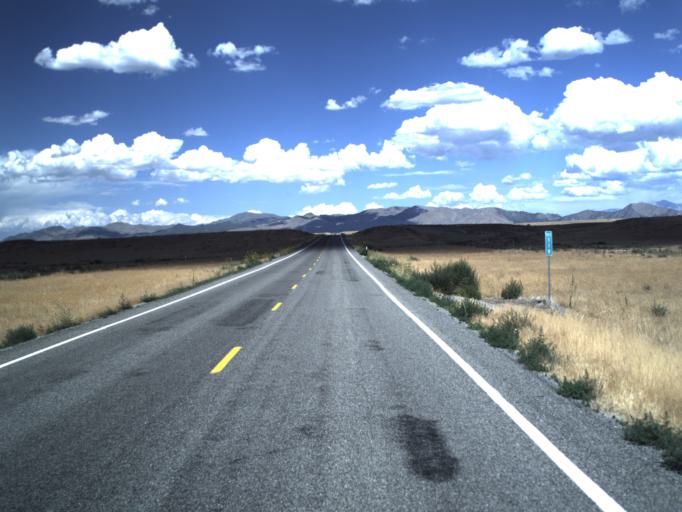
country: US
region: Utah
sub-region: Juab County
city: Nephi
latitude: 39.6800
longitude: -112.2526
